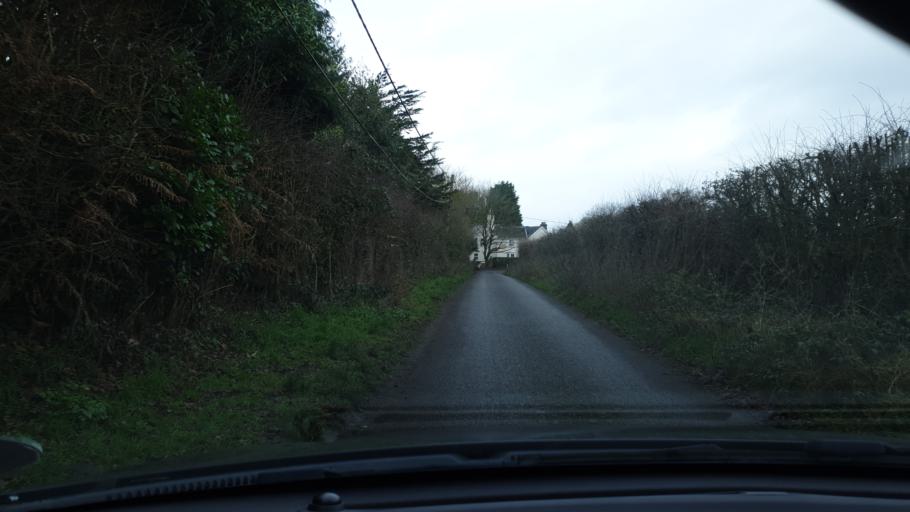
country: GB
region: England
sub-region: Essex
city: Alresford
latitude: 51.8574
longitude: 0.9927
